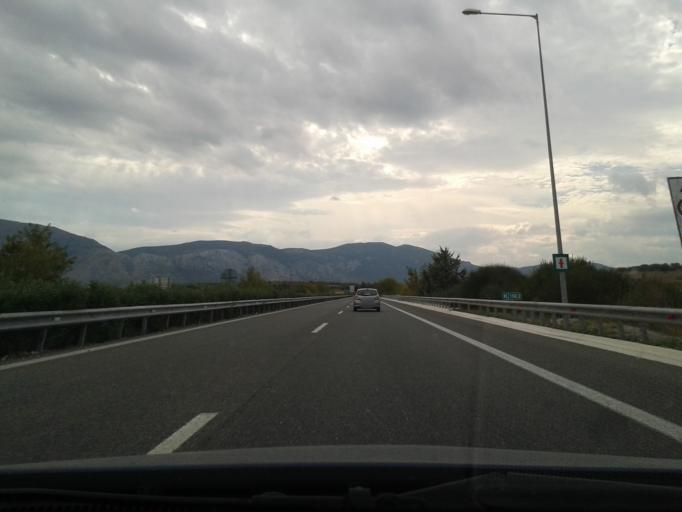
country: GR
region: Peloponnese
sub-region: Nomos Korinthias
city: Ayios Vasilios
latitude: 37.8329
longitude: 22.8060
